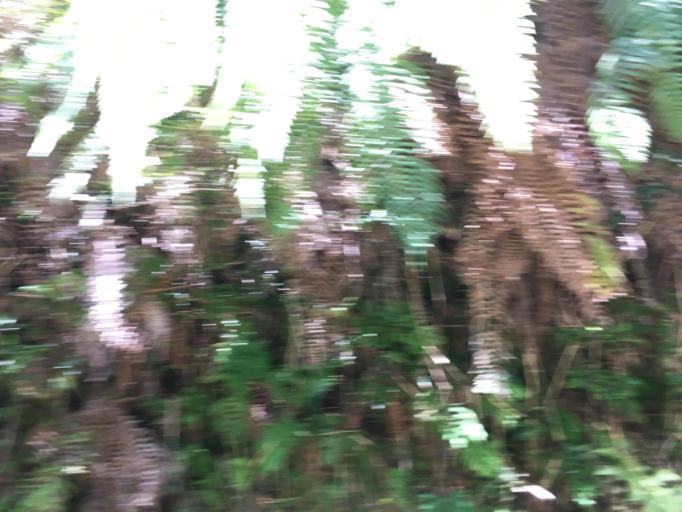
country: TW
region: Taiwan
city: Daxi
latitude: 24.5500
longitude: 121.3989
